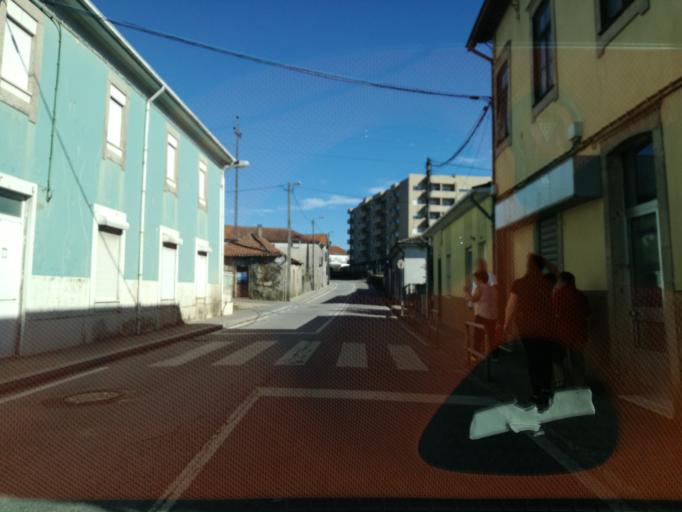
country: PT
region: Porto
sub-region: Trofa
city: Sao Romao do Coronado
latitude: 41.2789
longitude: -8.5519
